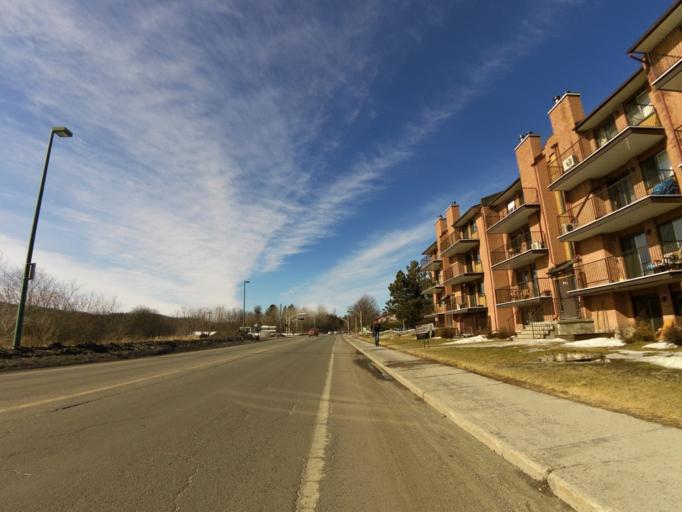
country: CA
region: Quebec
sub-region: Outaouais
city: Gatineau
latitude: 45.4500
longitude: -75.7562
